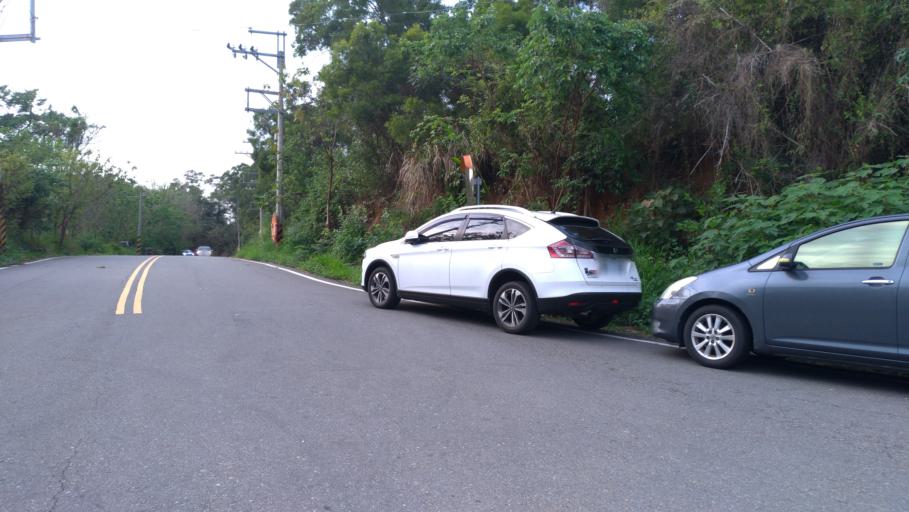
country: TW
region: Taiwan
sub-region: Hsinchu
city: Hsinchu
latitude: 24.7535
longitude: 120.9909
